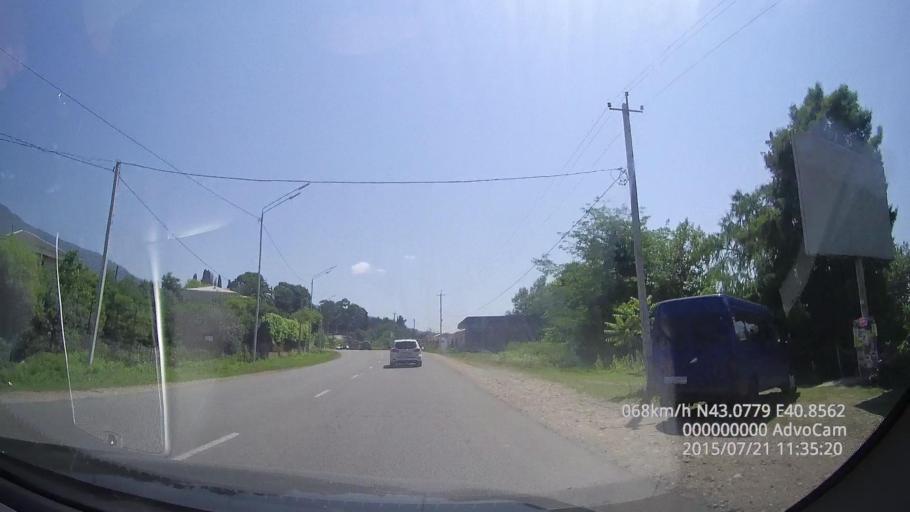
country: GE
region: Abkhazia
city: Stantsiya Novyy Afon
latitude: 43.0779
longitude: 40.8567
